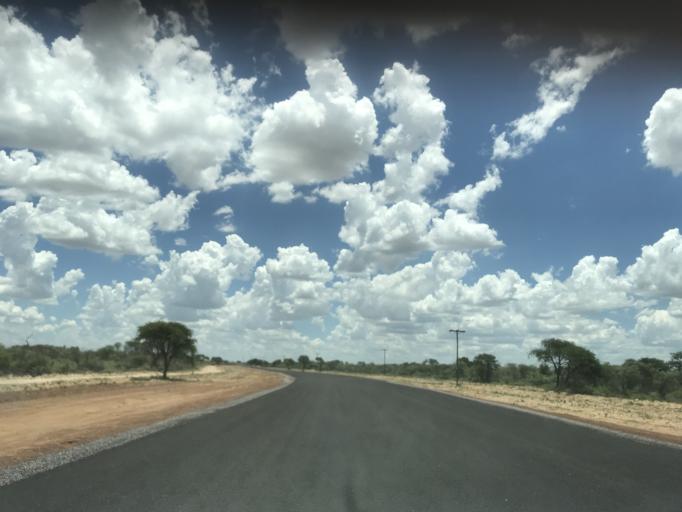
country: BW
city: Mabuli
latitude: -25.7979
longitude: 24.6682
